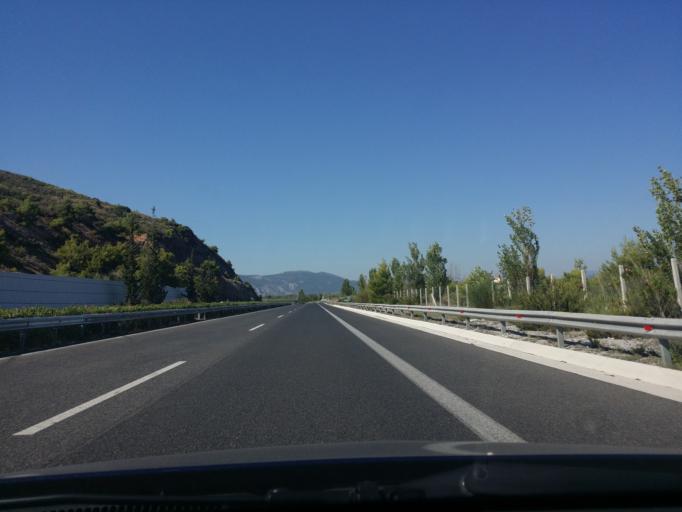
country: GR
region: Peloponnese
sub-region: Nomos Korinthias
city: Khiliomodhi
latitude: 37.8564
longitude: 22.8335
